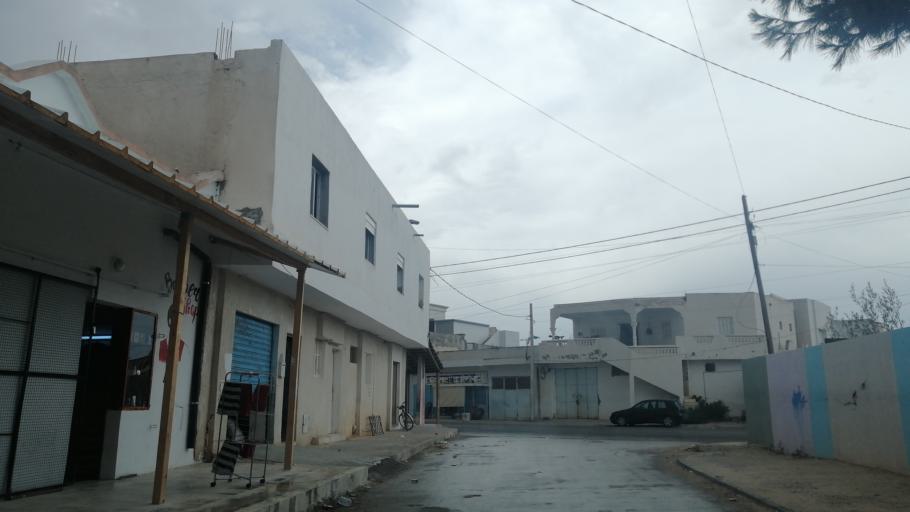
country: TN
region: Al Qayrawan
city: Sbikha
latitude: 36.1251
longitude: 10.0933
